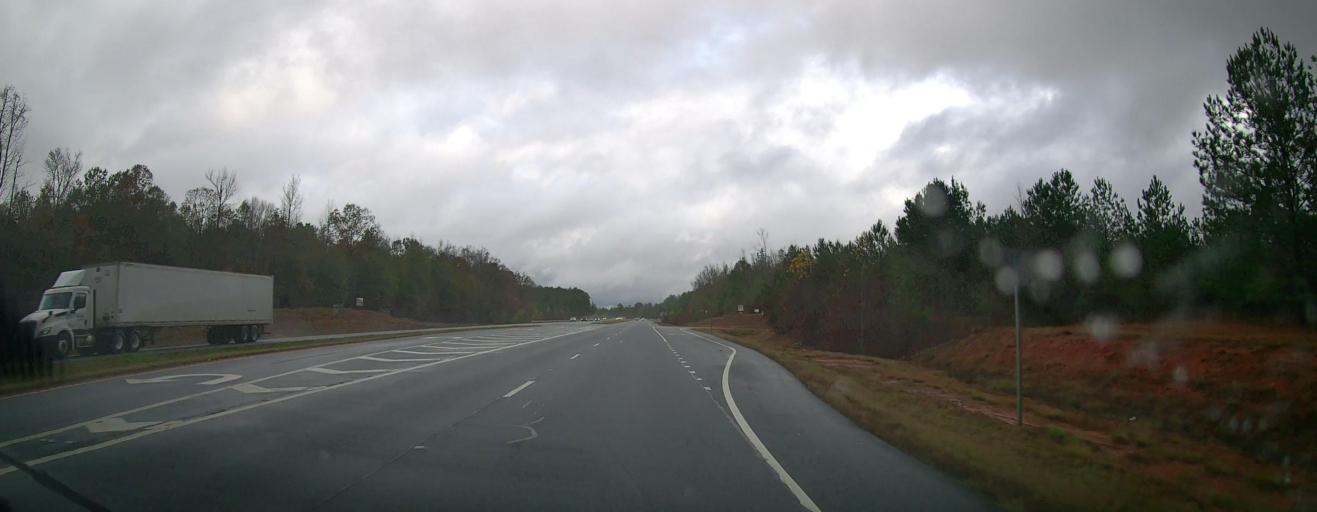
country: US
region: Georgia
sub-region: Jackson County
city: Nicholson
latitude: 34.0689
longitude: -83.4249
